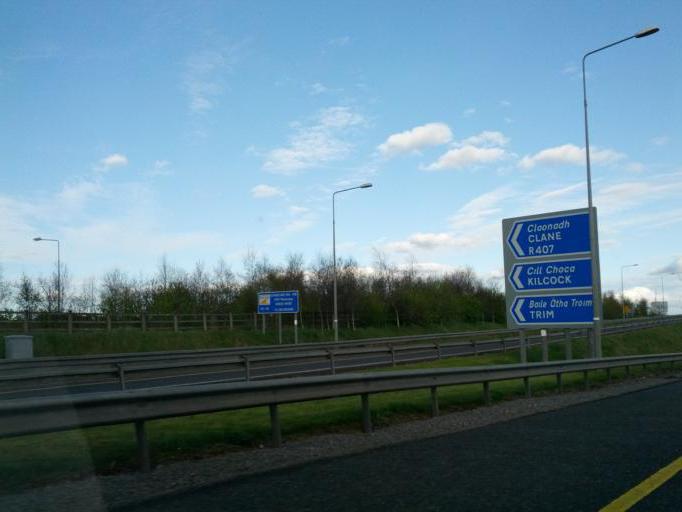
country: IE
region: Leinster
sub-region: Kildare
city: Kilcock
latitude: 53.4039
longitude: -6.6934
